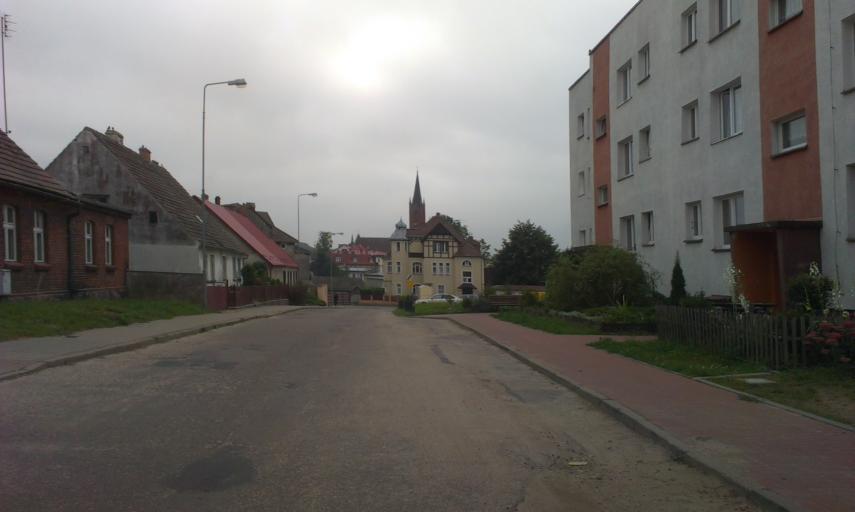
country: PL
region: West Pomeranian Voivodeship
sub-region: Powiat szczecinecki
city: Barwice
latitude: 53.7455
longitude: 16.3531
